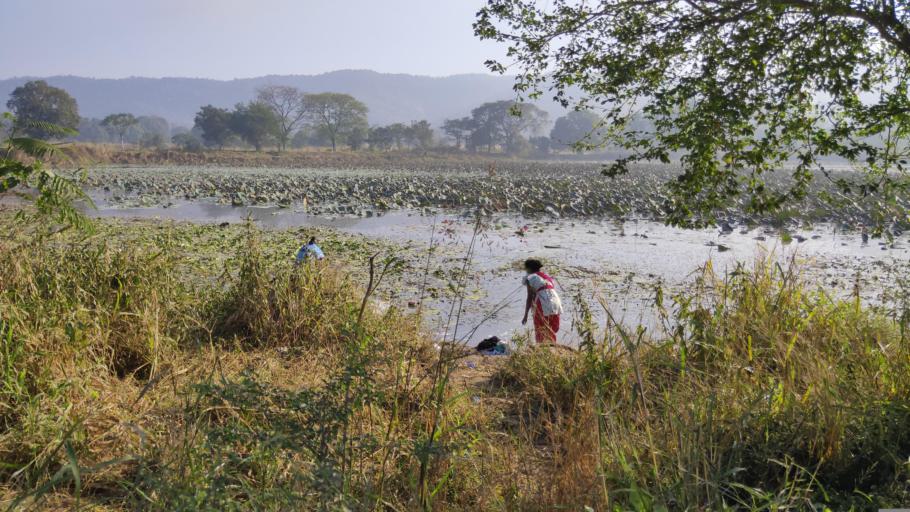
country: IN
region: Maharashtra
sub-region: Thane
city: Bhiwandi
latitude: 19.3269
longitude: 72.9774
